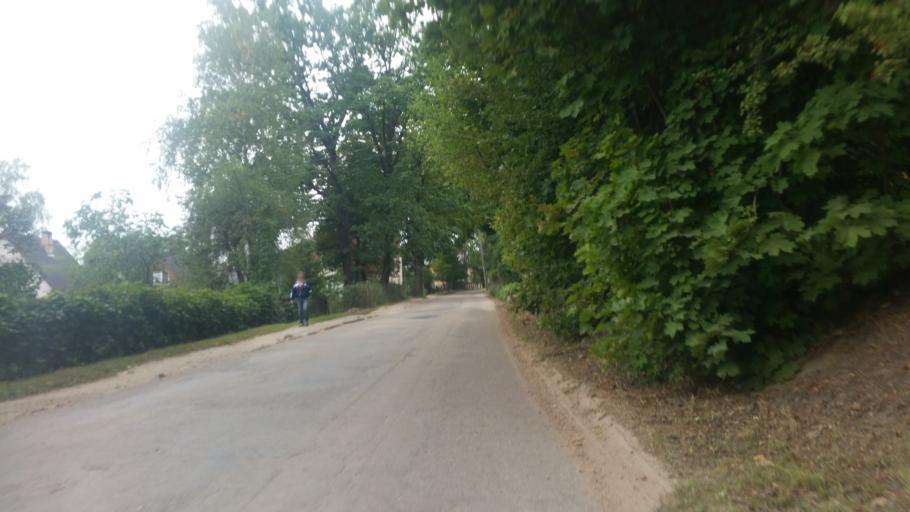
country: LV
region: Ogre
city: Ogre
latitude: 56.8099
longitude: 24.6188
